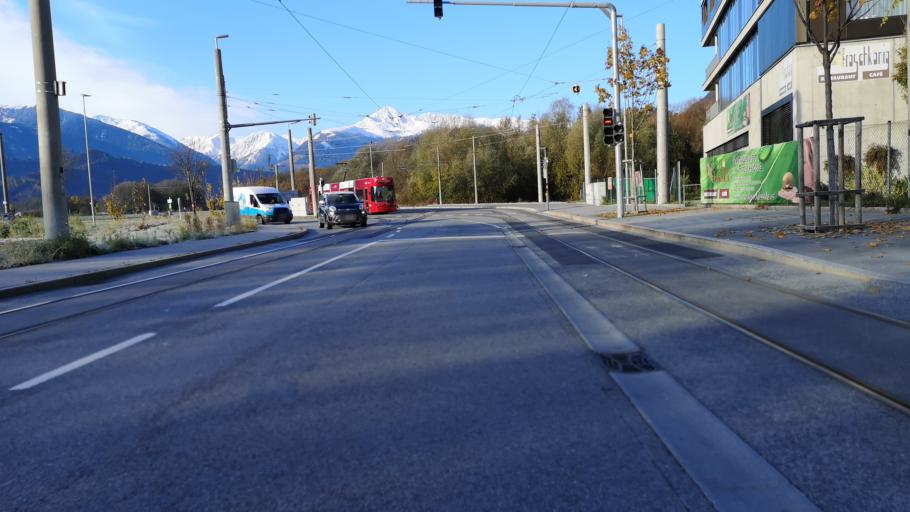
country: AT
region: Tyrol
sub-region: Politischer Bezirk Innsbruck Land
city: Vols
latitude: 47.2650
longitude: 11.3402
